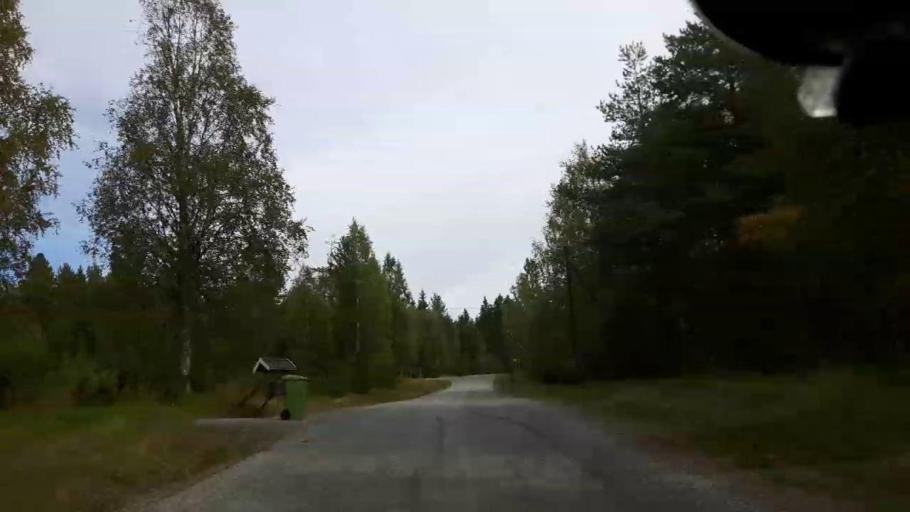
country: SE
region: Jaemtland
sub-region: Ragunda Kommun
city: Hammarstrand
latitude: 63.0105
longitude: 16.0984
